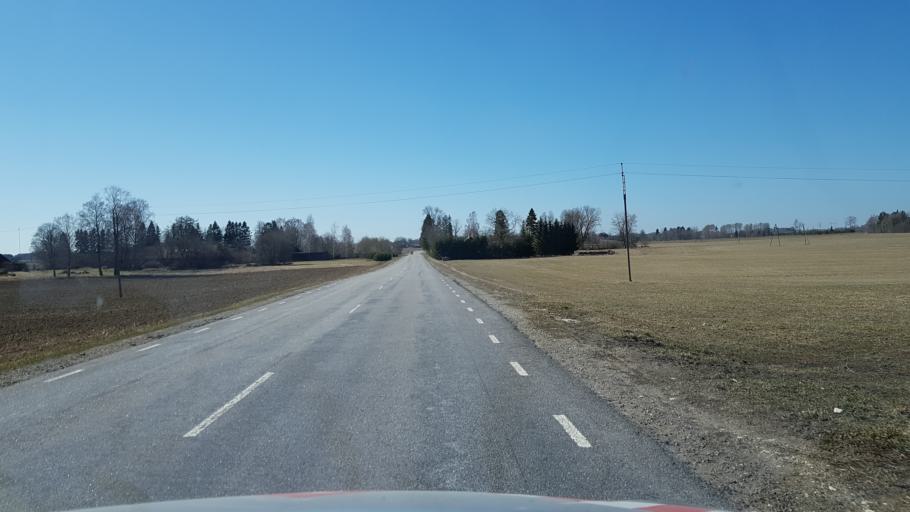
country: EE
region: Laeaene-Virumaa
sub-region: Tamsalu vald
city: Tamsalu
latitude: 59.1689
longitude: 26.1592
